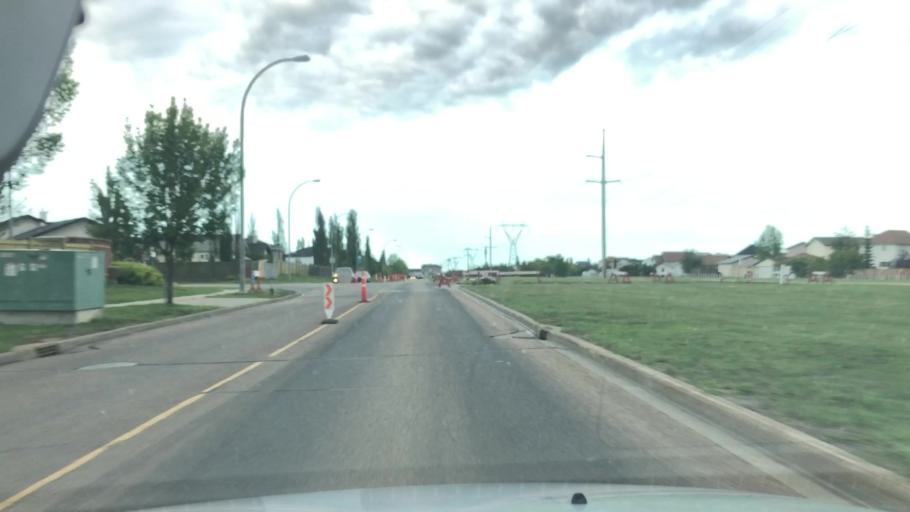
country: CA
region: Alberta
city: St. Albert
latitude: 53.6146
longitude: -113.5580
